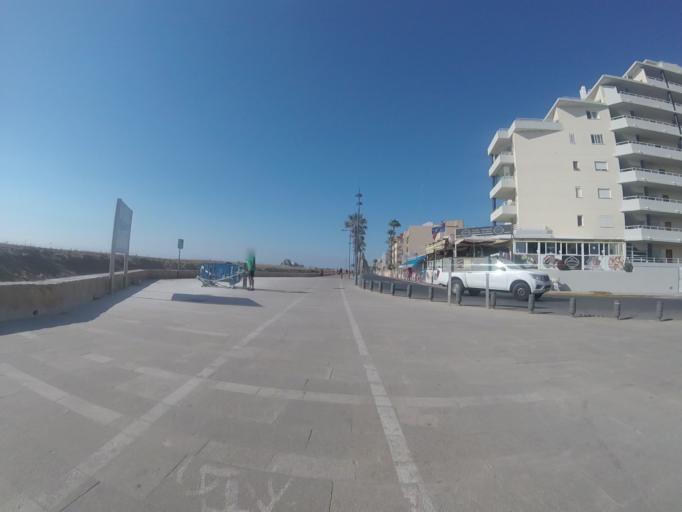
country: ES
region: Valencia
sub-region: Provincia de Castello
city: Peniscola
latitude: 40.3781
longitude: 0.4075
